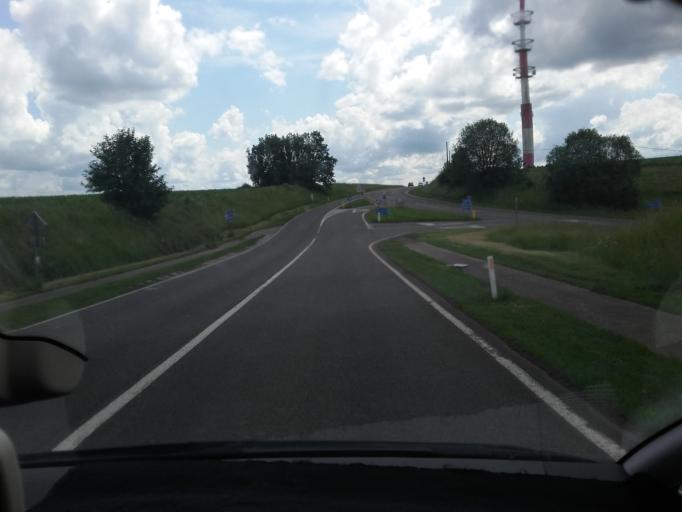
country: BE
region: Wallonia
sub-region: Province de Namur
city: Rochefort
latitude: 50.2349
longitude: 5.1846
